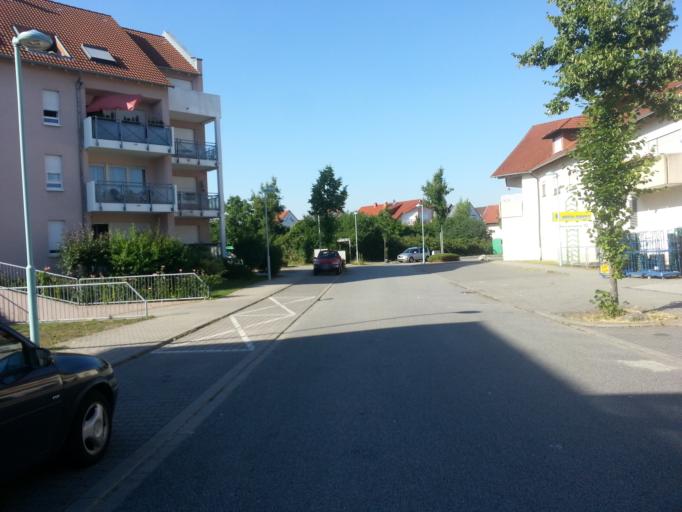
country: DE
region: Baden-Wuerttemberg
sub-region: Karlsruhe Region
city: Ilvesheim
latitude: 49.4632
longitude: 8.5532
